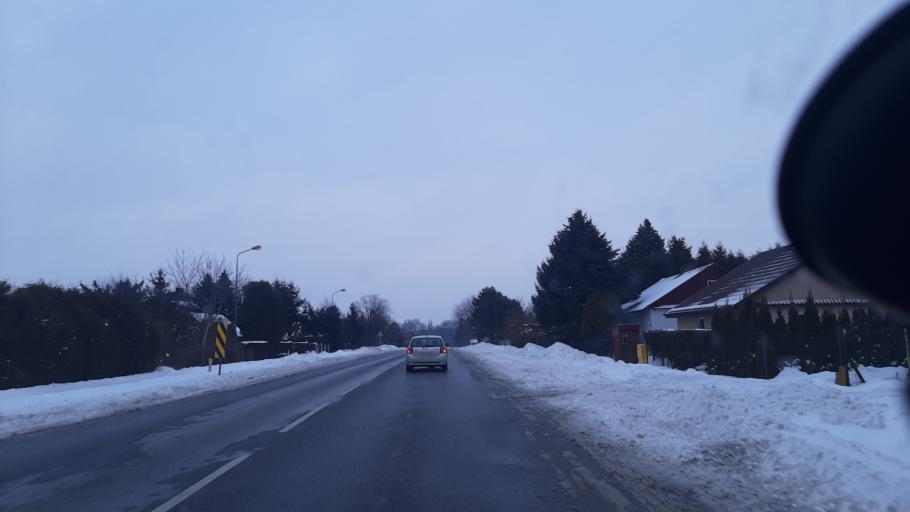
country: PL
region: Lublin Voivodeship
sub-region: Powiat lubelski
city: Garbow
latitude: 51.3577
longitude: 22.3205
